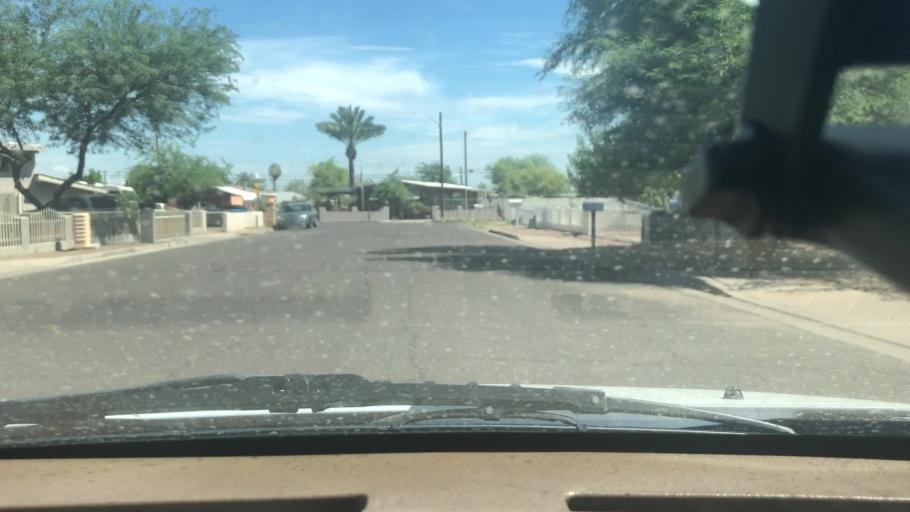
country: US
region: Arizona
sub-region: Maricopa County
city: Guadalupe
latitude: 33.3885
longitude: -112.0311
